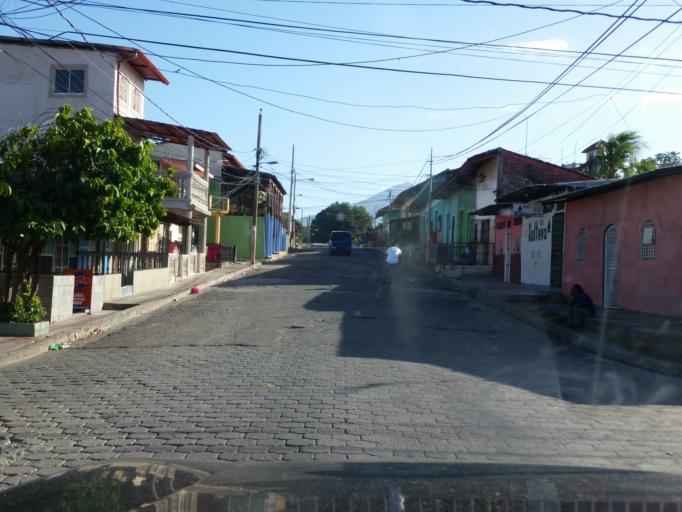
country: NI
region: Granada
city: Granada
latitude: 11.9268
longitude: -85.9604
